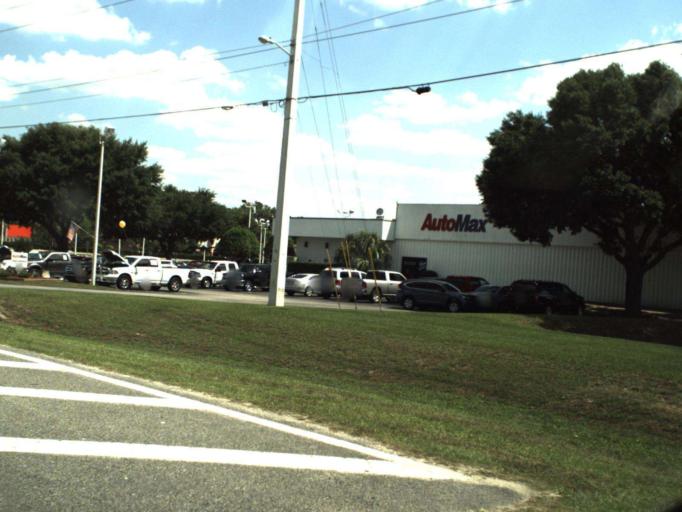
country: US
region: Florida
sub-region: Marion County
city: Ocala
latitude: 29.1716
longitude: -82.1579
